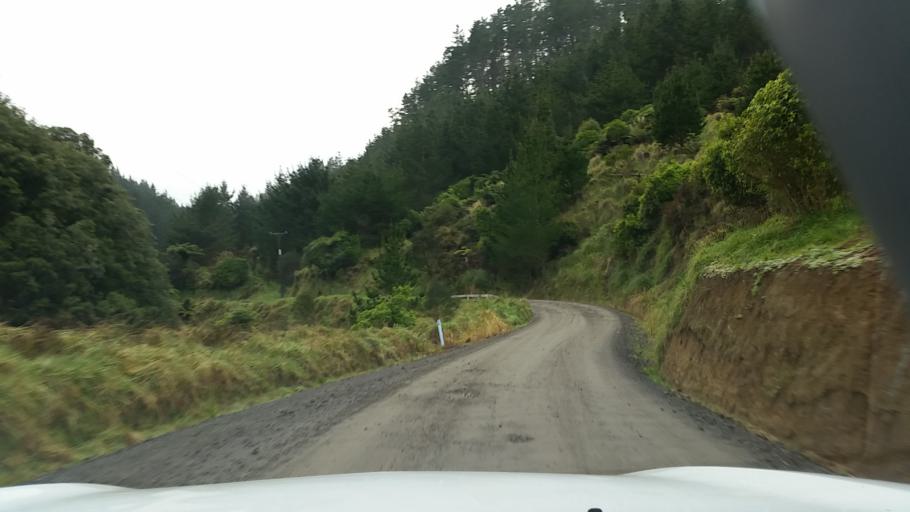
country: NZ
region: Taranaki
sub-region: South Taranaki District
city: Eltham
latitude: -39.5226
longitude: 174.4142
